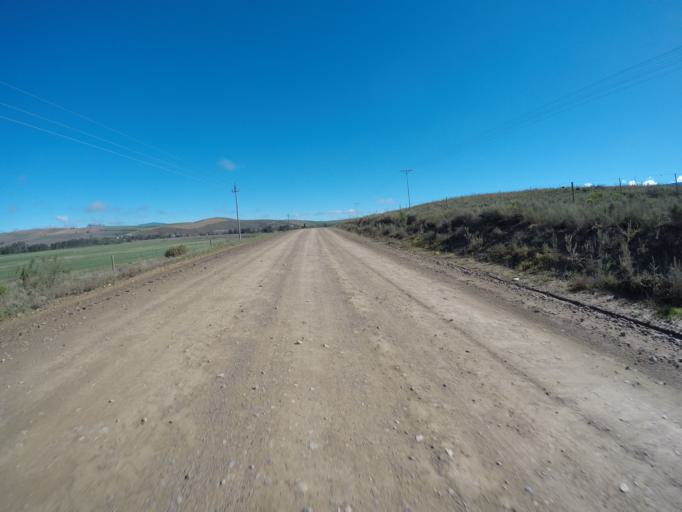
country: ZA
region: Western Cape
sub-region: Overberg District Municipality
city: Caledon
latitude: -34.0967
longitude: 19.6785
